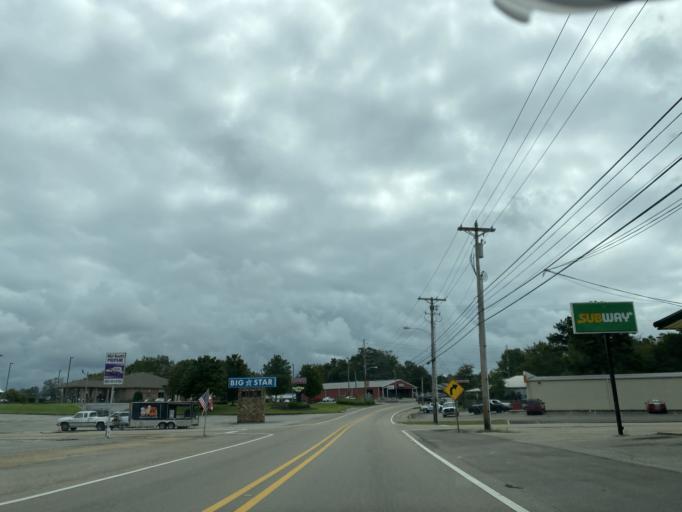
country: US
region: Mississippi
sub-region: Tishomingo County
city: Belmont
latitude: 34.5082
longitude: -88.2079
